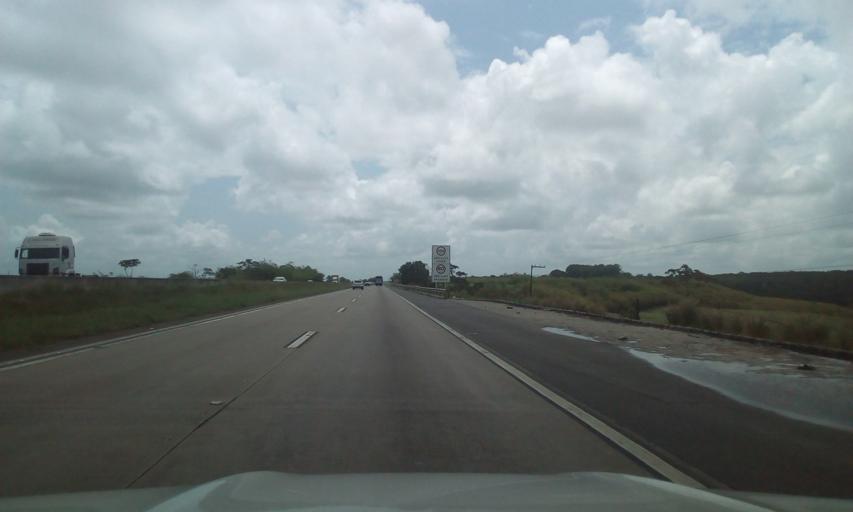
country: BR
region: Pernambuco
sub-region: Goiana
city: Goiana
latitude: -7.6553
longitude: -34.9426
